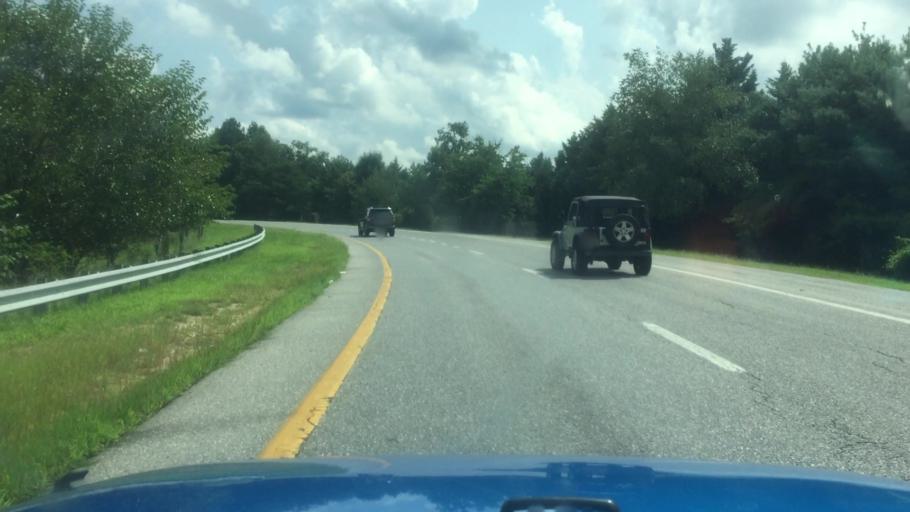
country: US
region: Maryland
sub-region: Anne Arundel County
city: South Gate
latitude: 39.0932
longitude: -76.6293
